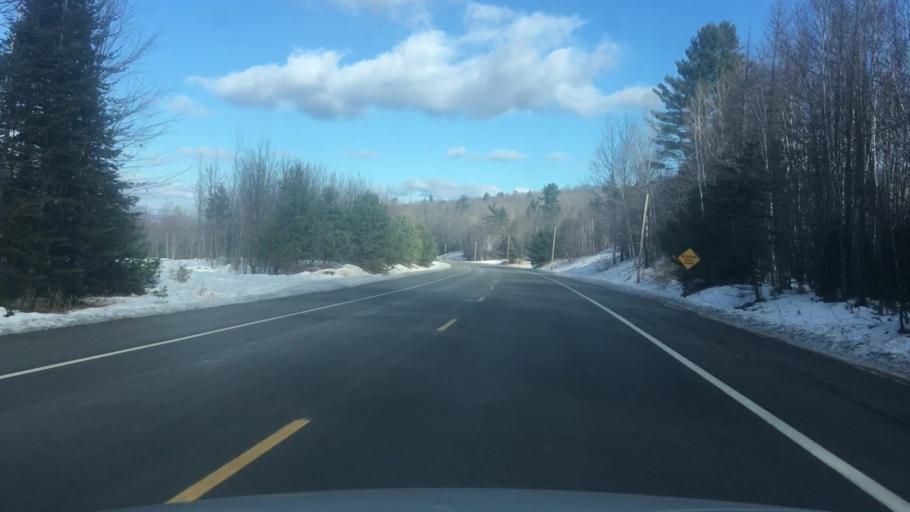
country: US
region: Maine
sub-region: Somerset County
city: Madison
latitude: 44.9984
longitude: -69.8595
